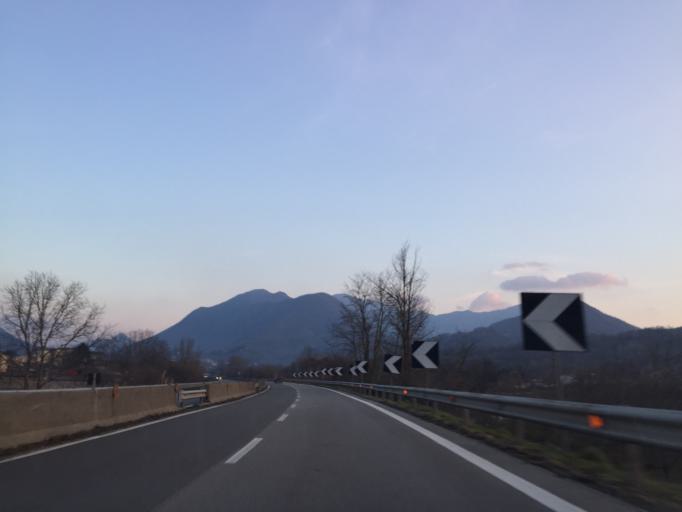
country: IT
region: Campania
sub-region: Provincia di Avellino
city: San Michele di Serino
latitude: 40.8761
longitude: 14.8512
